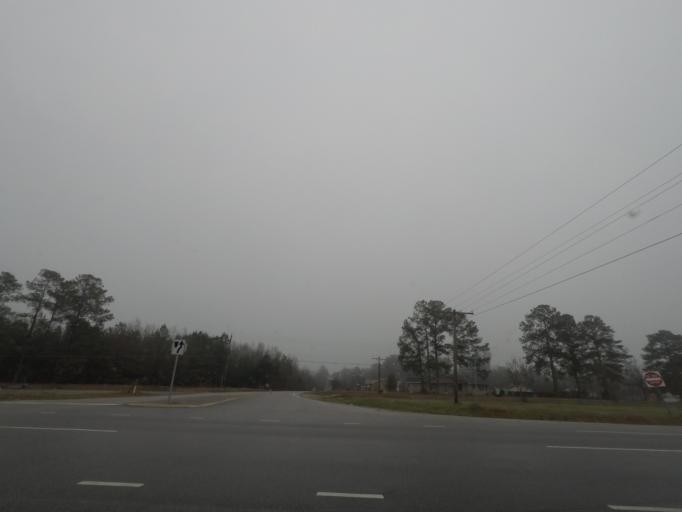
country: US
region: North Carolina
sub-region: Scotland County
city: Laurinburg
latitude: 34.8038
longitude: -79.4382
